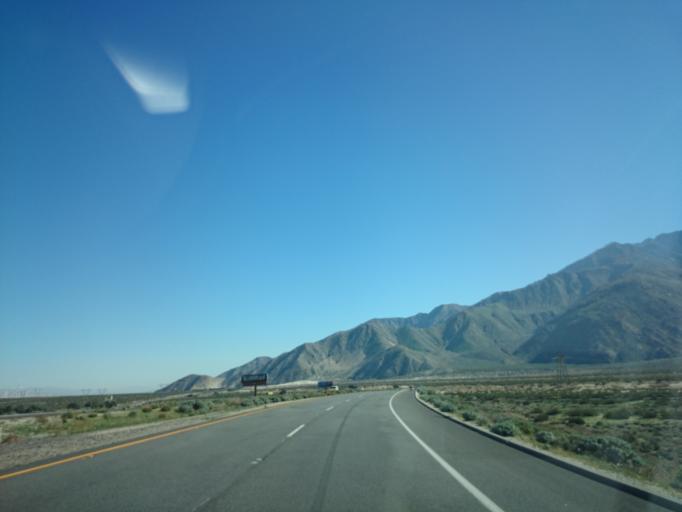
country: US
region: California
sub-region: Riverside County
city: Cabazon
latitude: 33.9208
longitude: -116.6766
